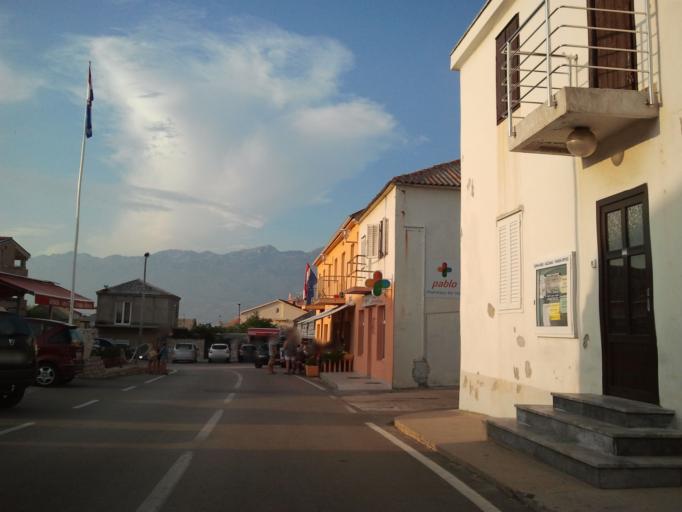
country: HR
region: Zadarska
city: Razanac
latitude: 44.2823
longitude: 15.3477
